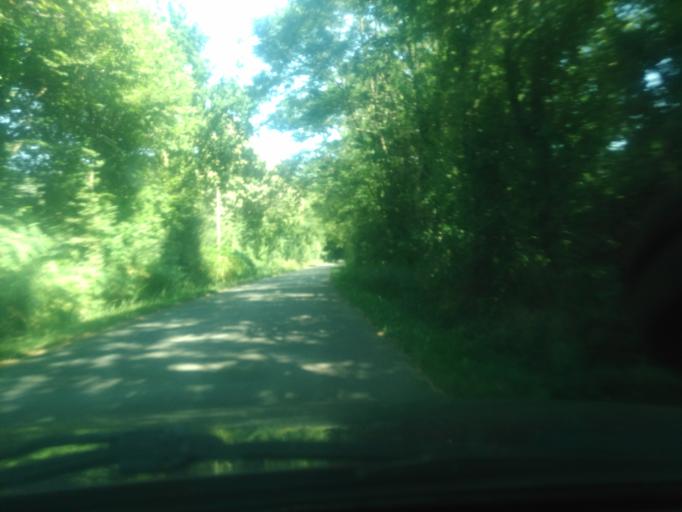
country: FR
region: Pays de la Loire
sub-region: Departement de la Vendee
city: Dompierre-sur-Yon
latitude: 46.7223
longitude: -1.3690
